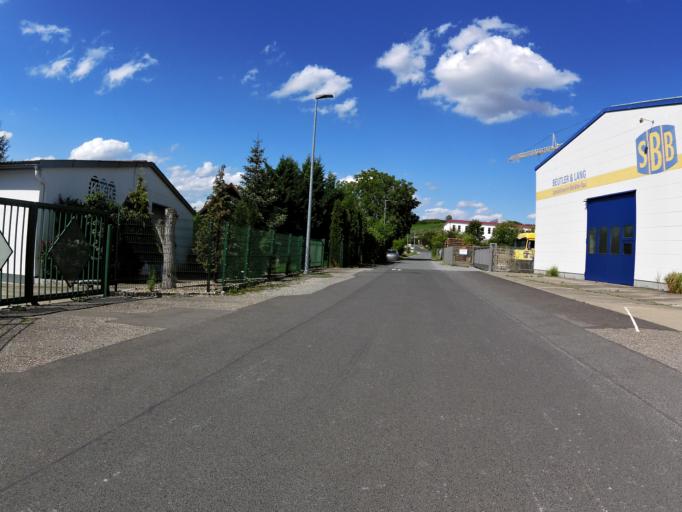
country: DE
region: Bavaria
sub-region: Regierungsbezirk Unterfranken
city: Segnitz
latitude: 49.6775
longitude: 10.1526
